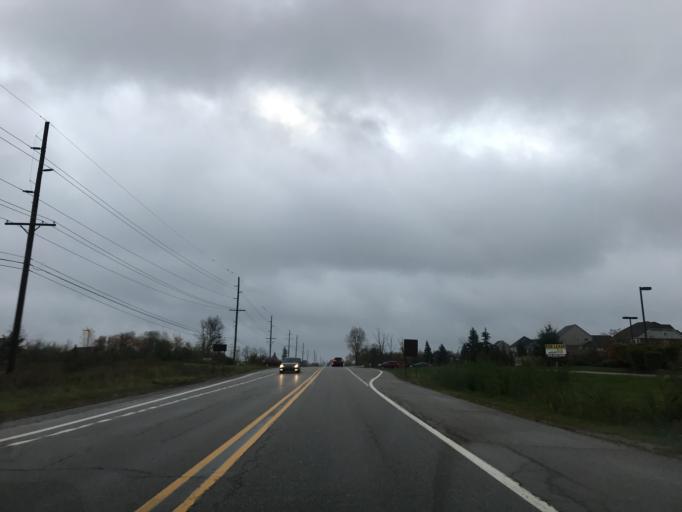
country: US
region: Michigan
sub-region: Oakland County
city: Wixom
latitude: 42.4639
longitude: -83.5606
